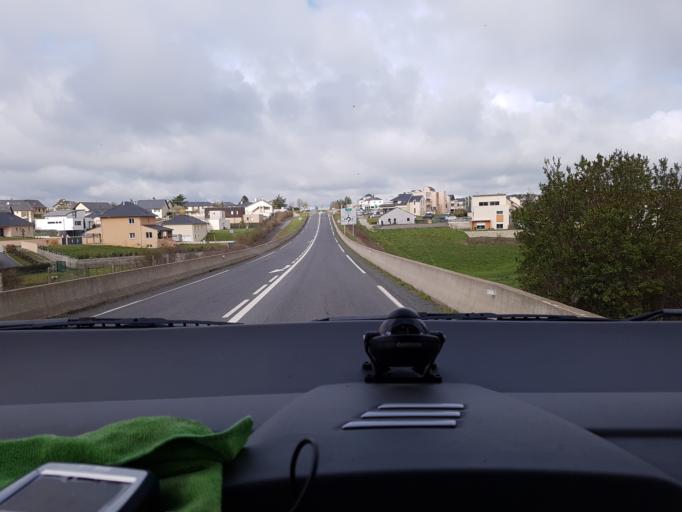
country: FR
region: Midi-Pyrenees
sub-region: Departement de l'Aveyron
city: Druelle
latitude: 44.3690
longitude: 2.5213
